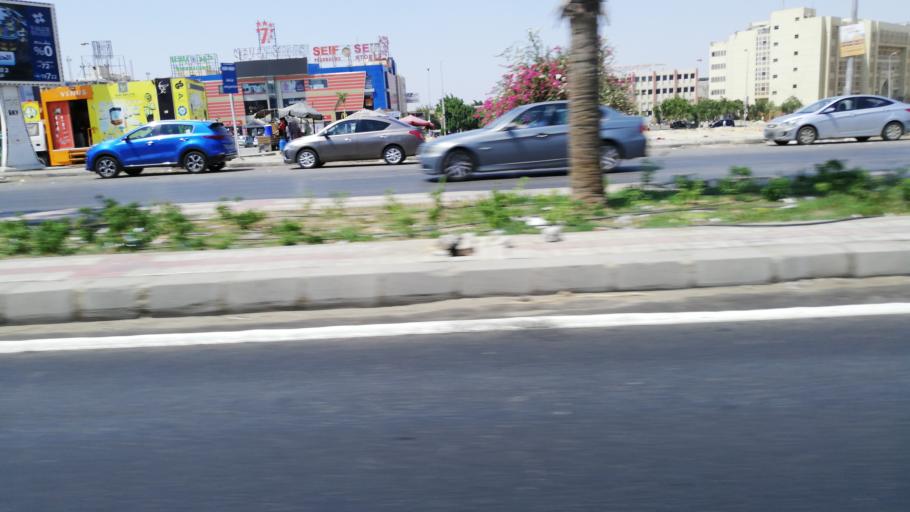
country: EG
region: Muhafazat al Qahirah
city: Cairo
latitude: 30.0033
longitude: 31.4260
